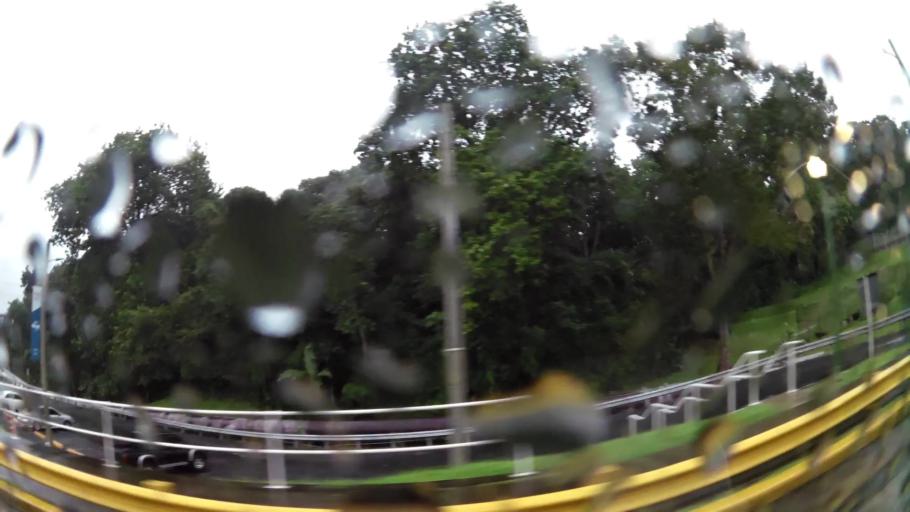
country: PA
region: Panama
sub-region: Distrito de Panama
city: Paraiso
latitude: 9.0015
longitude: -79.5915
